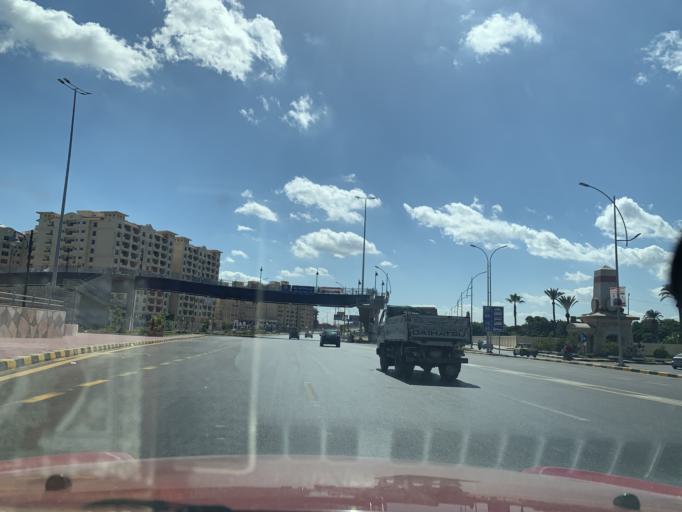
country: EG
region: Alexandria
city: Alexandria
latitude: 31.2045
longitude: 29.9540
